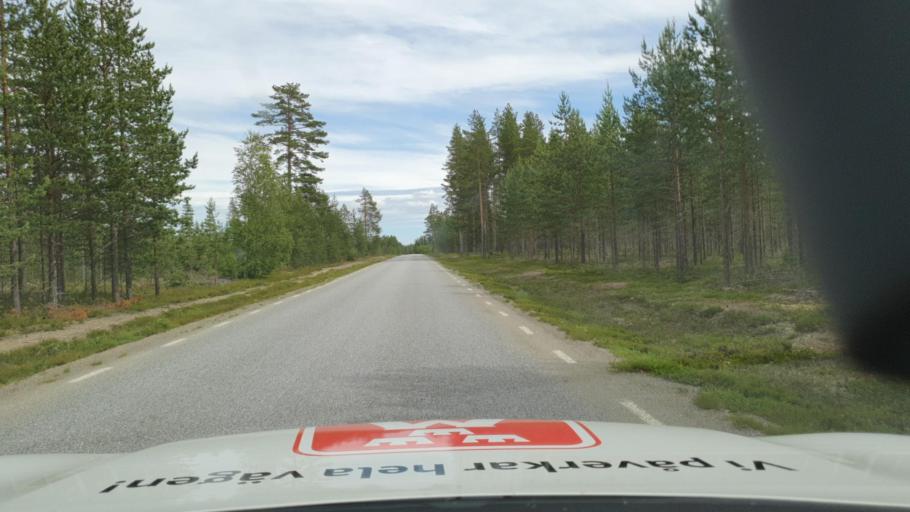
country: SE
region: Vaesterbotten
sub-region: Skelleftea Kommun
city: Burtraesk
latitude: 64.5041
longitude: 20.8172
